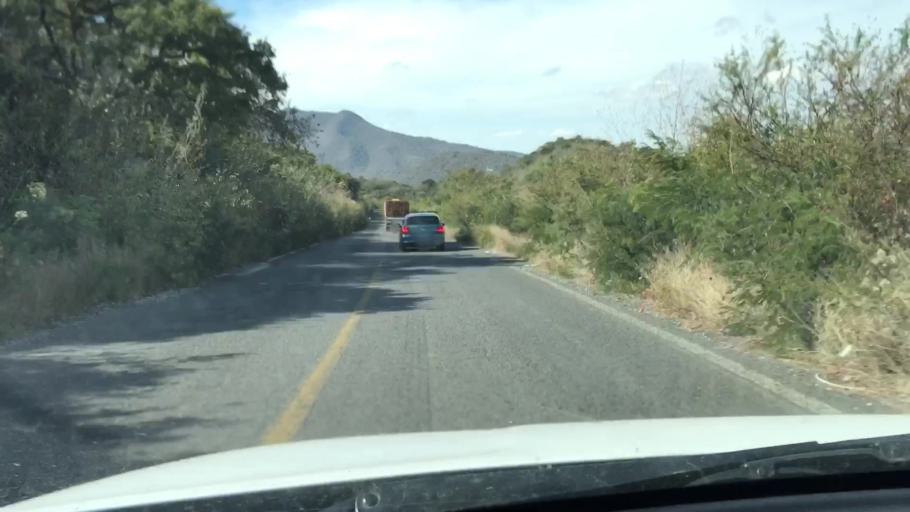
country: MX
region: Jalisco
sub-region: Zacoalco de Torres
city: Barranca de Otates (Barranca de Otatan)
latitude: 20.2279
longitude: -103.6785
